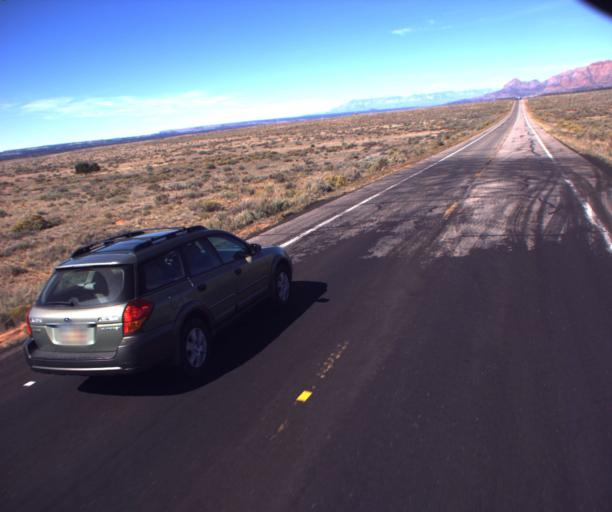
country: US
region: Arizona
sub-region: Mohave County
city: Colorado City
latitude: 36.9075
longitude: -112.9249
